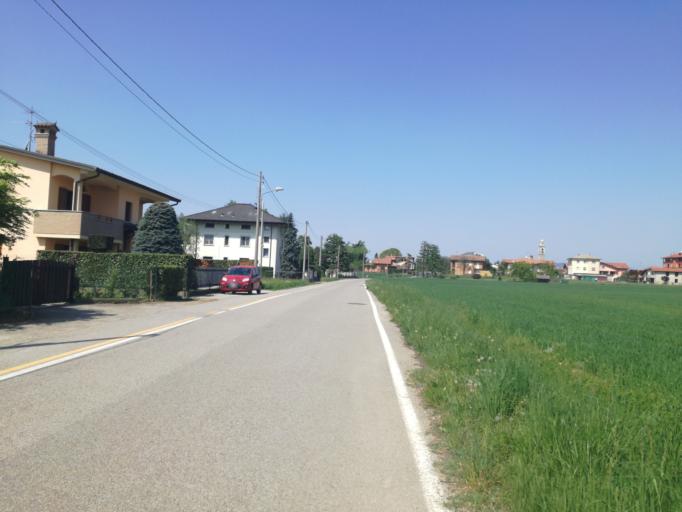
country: IT
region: Lombardy
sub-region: Provincia di Lecco
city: Verderio Superiore
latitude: 45.6594
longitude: 9.4407
